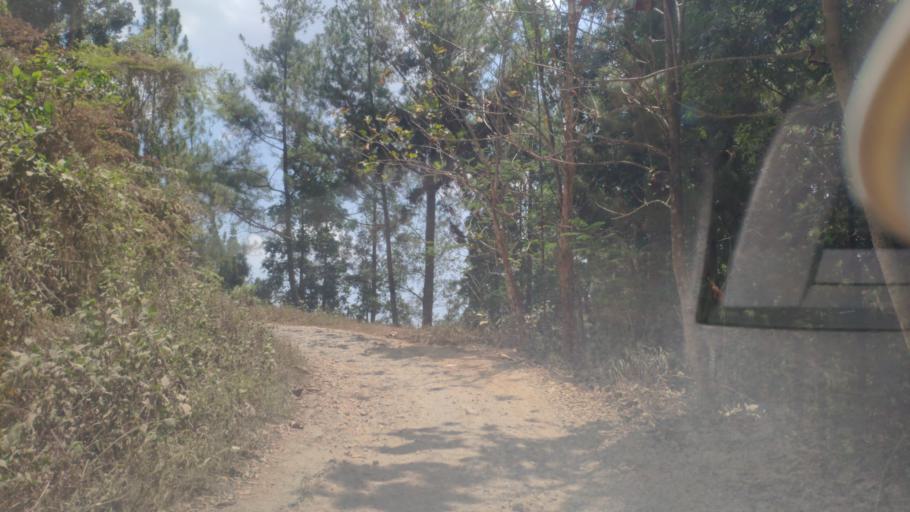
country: ID
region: Central Java
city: Gombong
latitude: -7.4833
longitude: 109.6146
